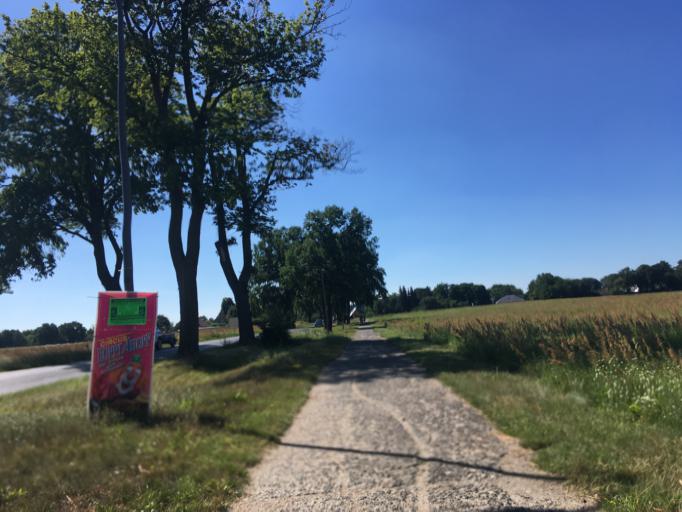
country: DE
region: Brandenburg
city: Petershagen
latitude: 52.5187
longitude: 13.7699
